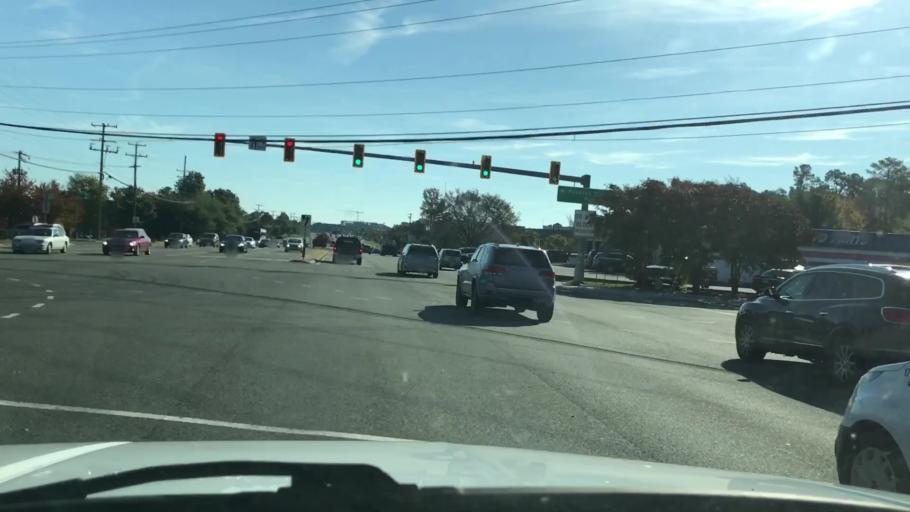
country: US
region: Virginia
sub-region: Henrico County
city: Short Pump
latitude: 37.6514
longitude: -77.6120
